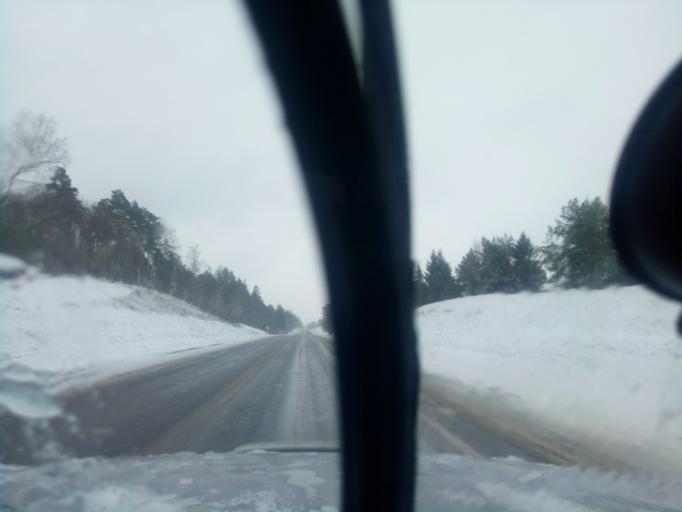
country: BY
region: Minsk
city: Haradzyeya
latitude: 53.2677
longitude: 26.6034
